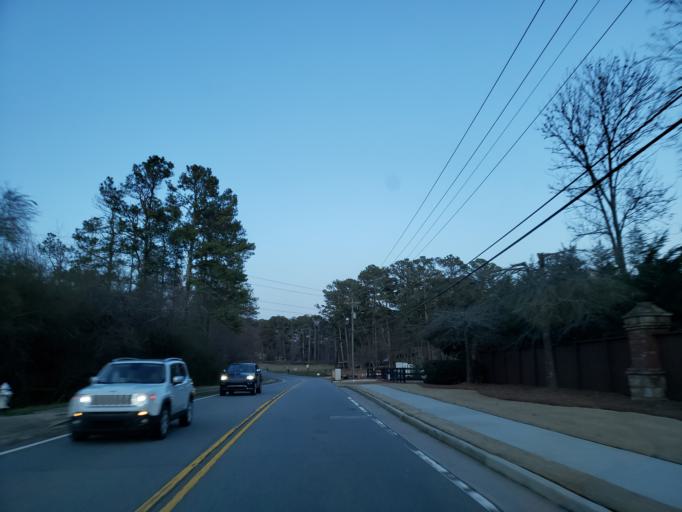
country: US
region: Georgia
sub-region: Cobb County
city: Kennesaw
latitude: 33.9942
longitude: -84.6577
